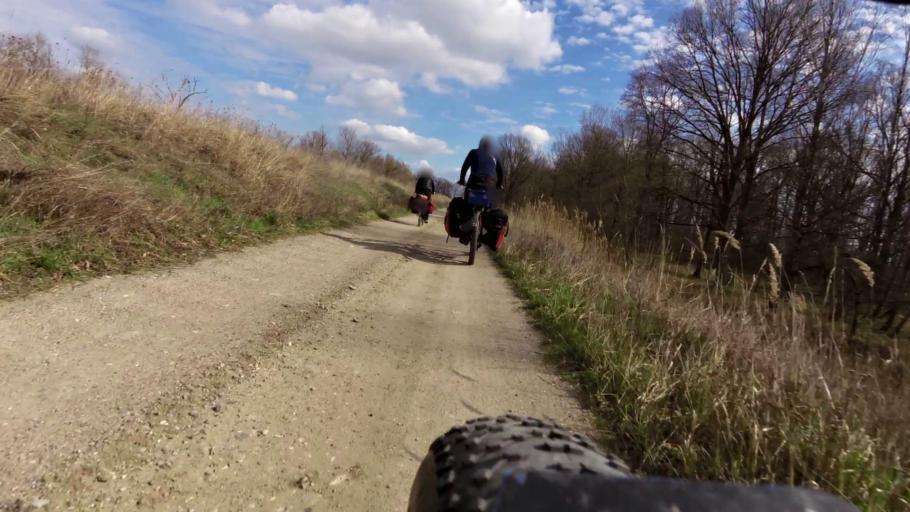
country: DE
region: Brandenburg
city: Lebus
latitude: 52.4370
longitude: 14.5690
